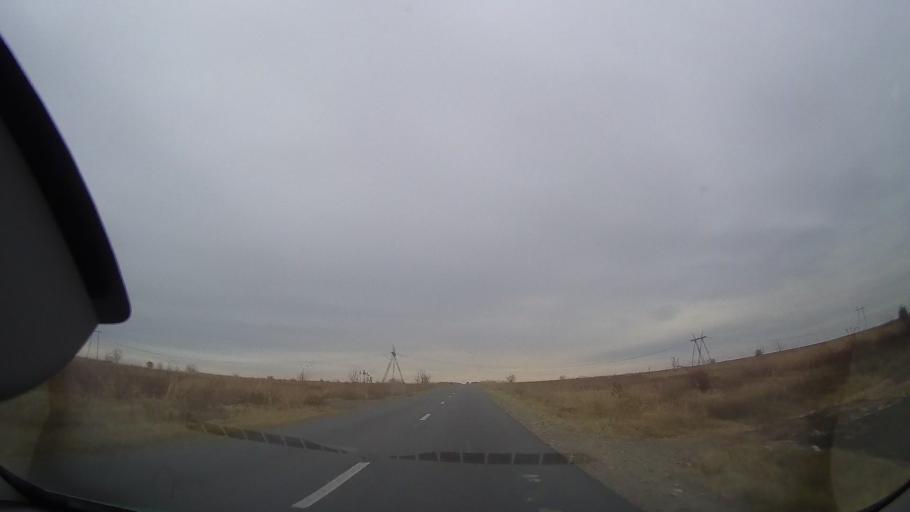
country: RO
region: Ialomita
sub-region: Oras Amara
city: Amara
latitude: 44.6372
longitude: 27.3008
